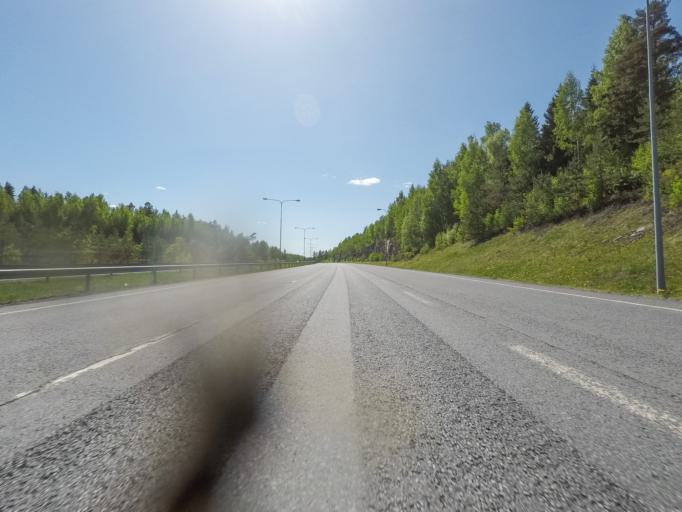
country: FI
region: Pirkanmaa
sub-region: Etelae-Pirkanmaa
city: Toijala
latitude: 61.1955
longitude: 23.8153
